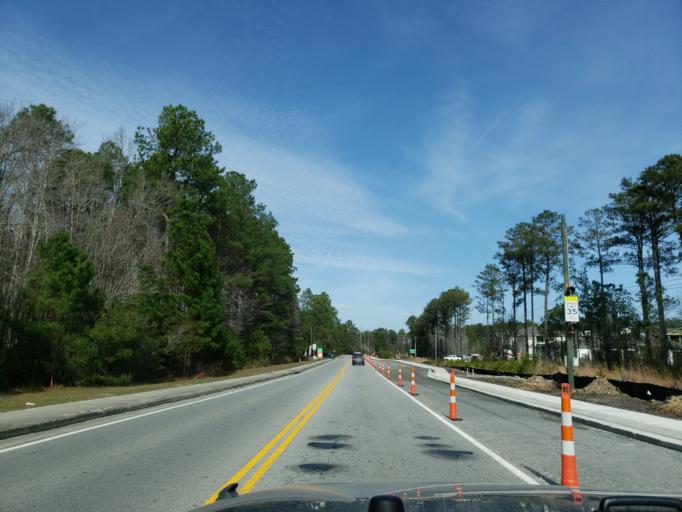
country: US
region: Georgia
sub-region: Chatham County
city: Pooler
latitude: 32.1696
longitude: -81.2340
